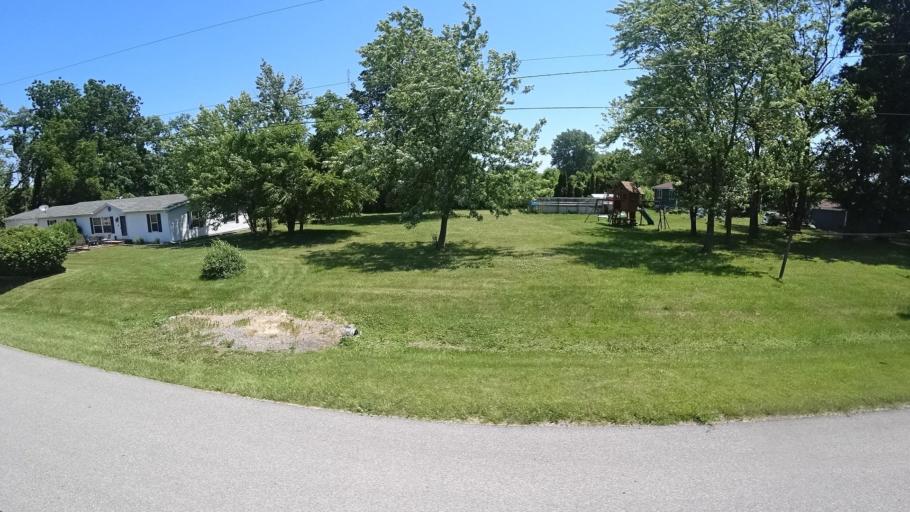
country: US
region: Indiana
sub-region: Porter County
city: Burns Harbor
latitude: 41.6035
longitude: -87.1259
